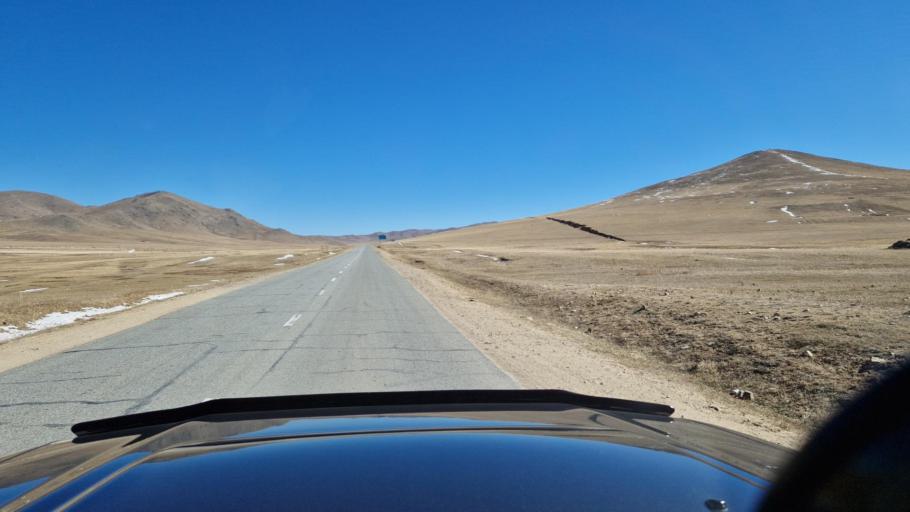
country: MN
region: Central Aimak
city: Bayandelger
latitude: 47.6928
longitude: 108.4781
